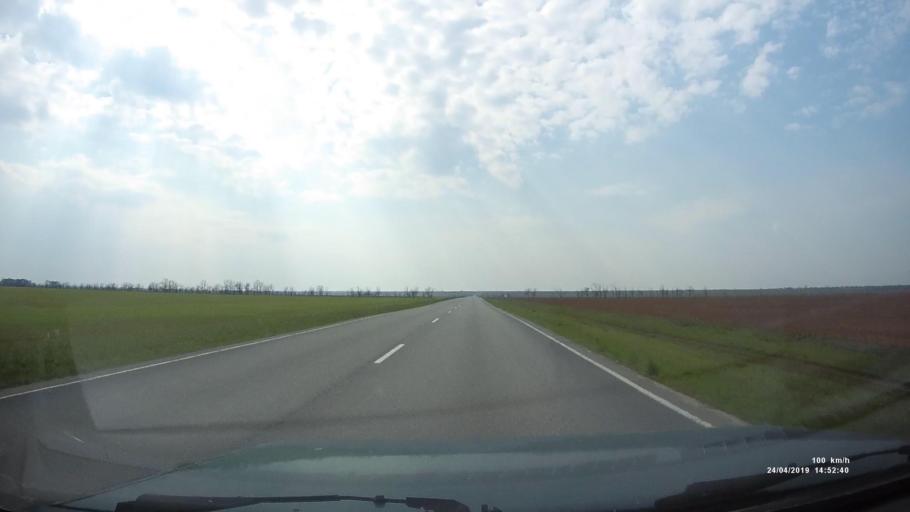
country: RU
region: Rostov
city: Remontnoye
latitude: 46.5305
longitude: 43.6756
